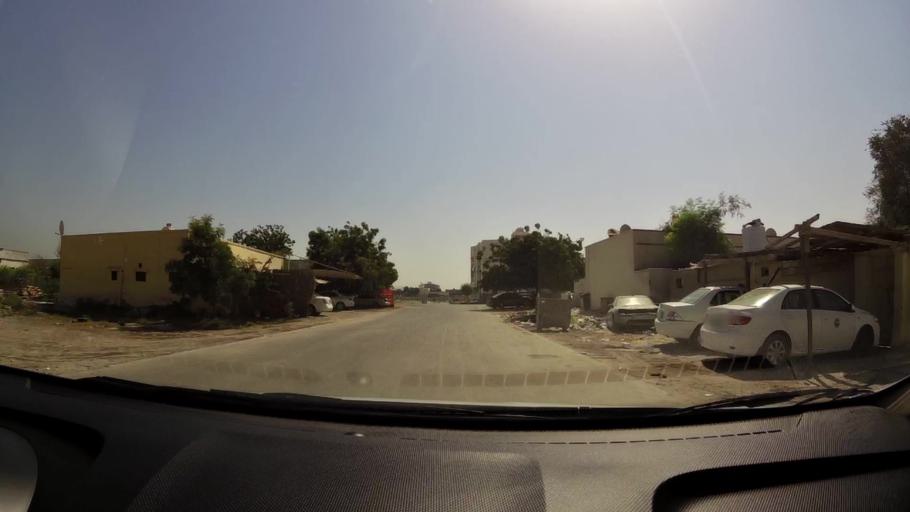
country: AE
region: Umm al Qaywayn
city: Umm al Qaywayn
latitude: 25.5886
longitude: 55.5757
